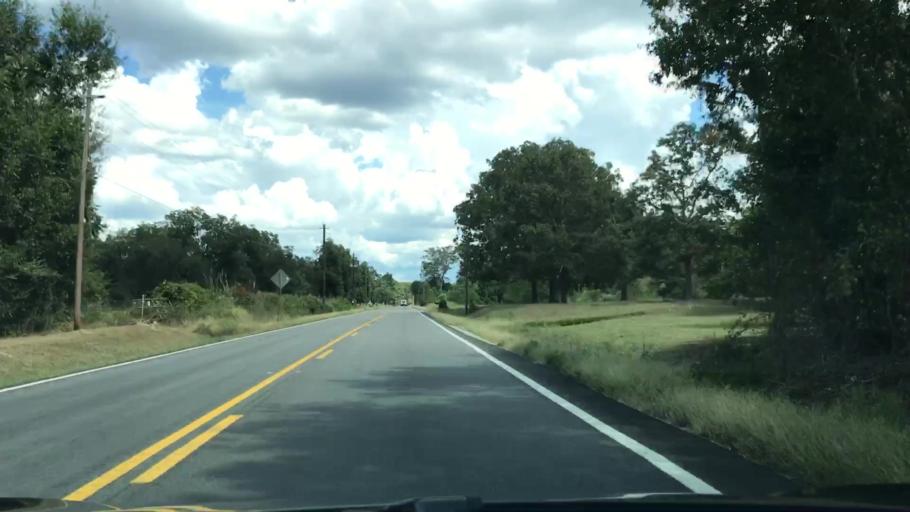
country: US
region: Georgia
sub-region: Greene County
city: Greensboro
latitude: 33.5591
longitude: -83.1295
